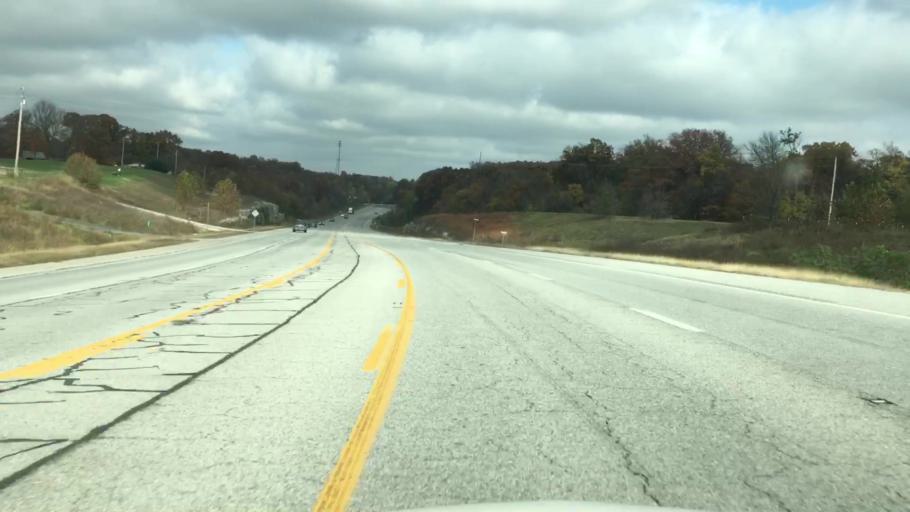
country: US
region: Arkansas
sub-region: Benton County
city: Gentry
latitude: 36.2378
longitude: -94.4874
